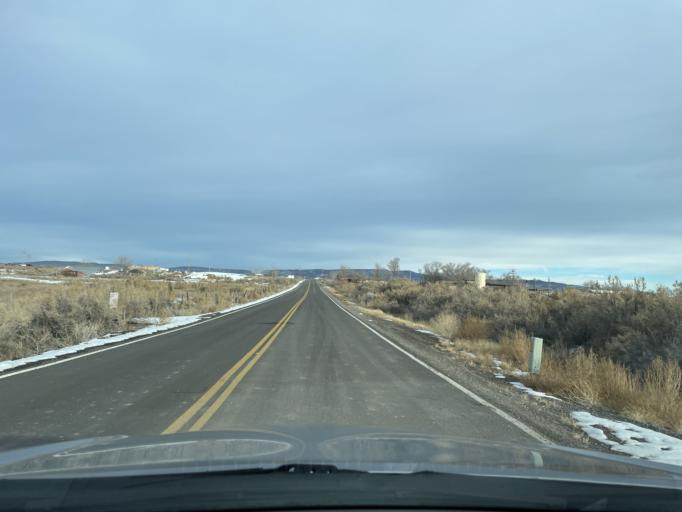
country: US
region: Colorado
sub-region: Montrose County
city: Olathe
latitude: 38.6497
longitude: -107.9951
